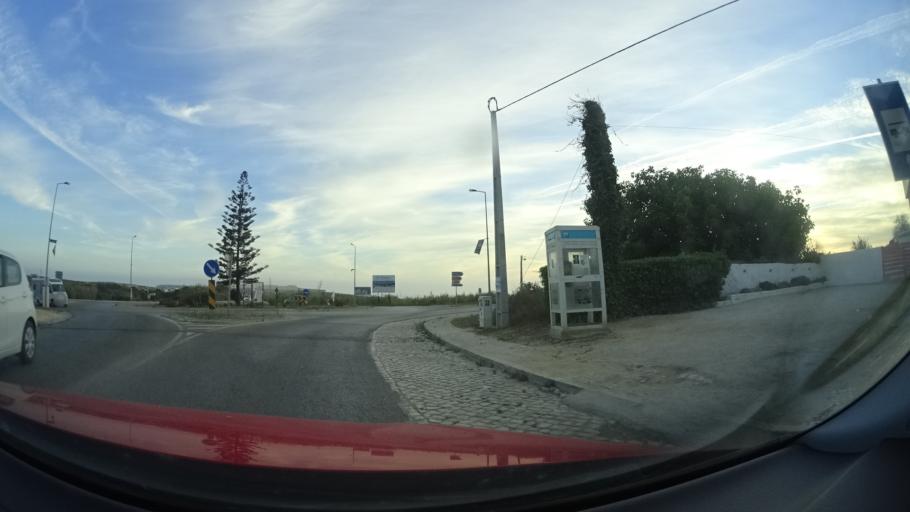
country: PT
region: Faro
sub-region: Vila do Bispo
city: Sagres
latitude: 37.0082
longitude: -8.9447
